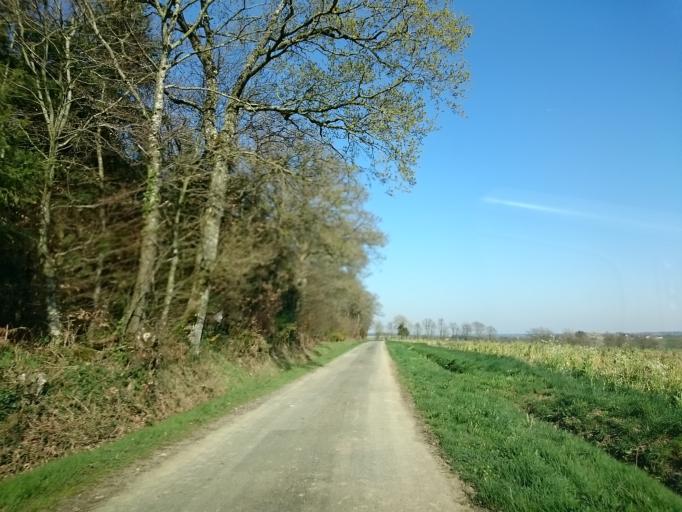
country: FR
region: Brittany
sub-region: Departement d'Ille-et-Vilaine
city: Chanteloup
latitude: 47.9540
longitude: -1.6275
